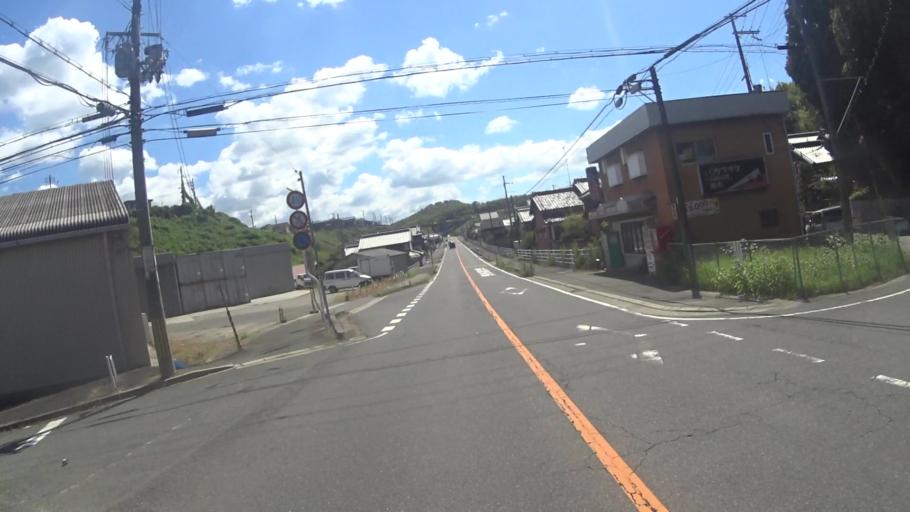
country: JP
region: Nara
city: Nara-shi
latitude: 34.7211
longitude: 135.8254
